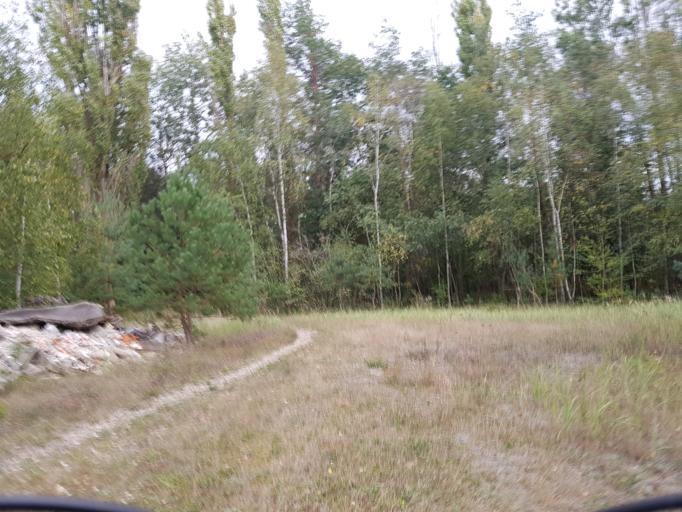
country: DE
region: Brandenburg
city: Trobitz
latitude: 51.5895
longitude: 13.4384
